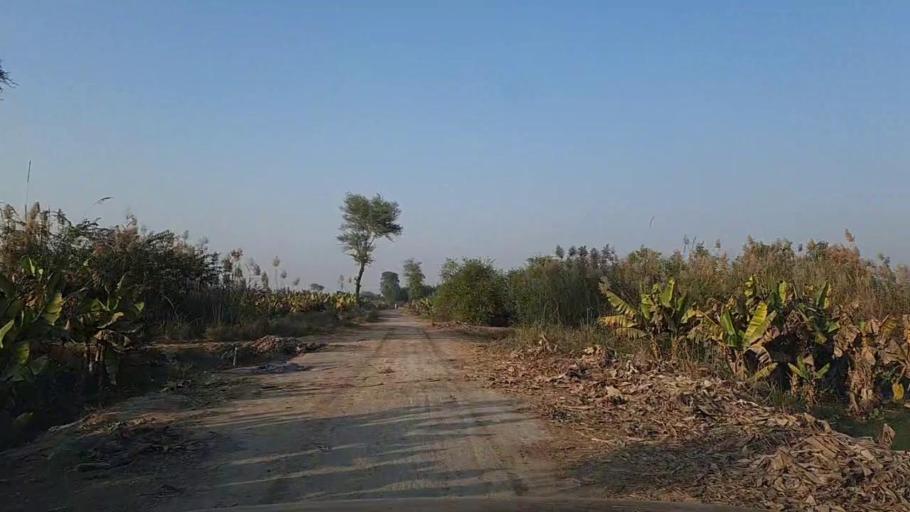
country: PK
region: Sindh
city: Daur
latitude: 26.4644
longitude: 68.3880
